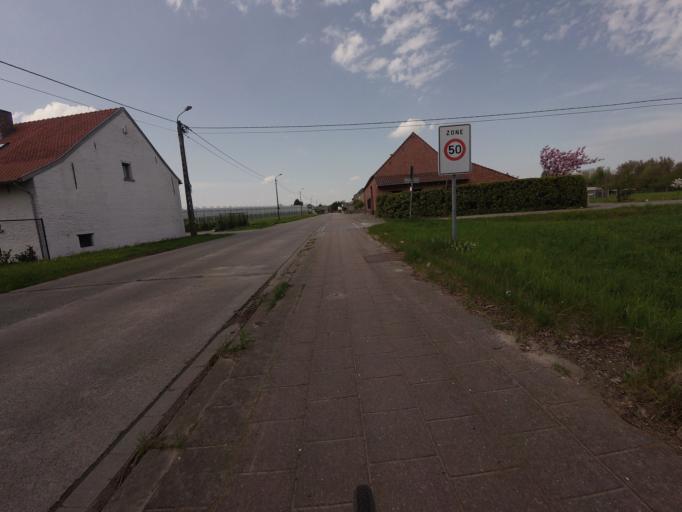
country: BE
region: Flanders
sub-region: Provincie Antwerpen
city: Putte
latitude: 51.0790
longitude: 4.5963
